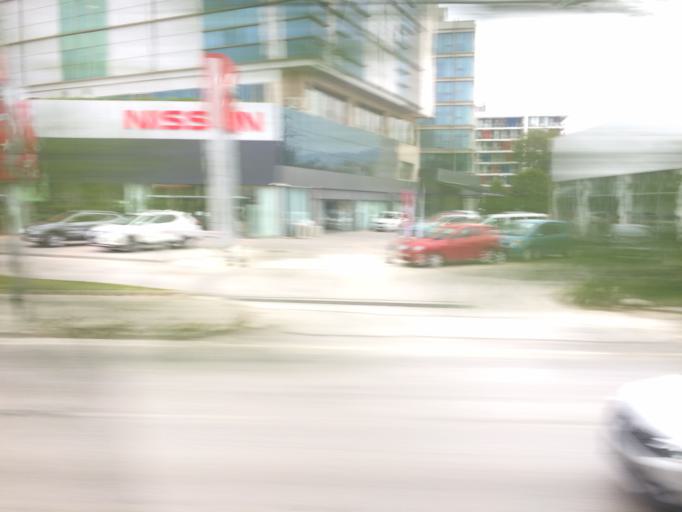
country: TR
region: Izmir
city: Buca
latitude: 38.4512
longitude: 27.1886
